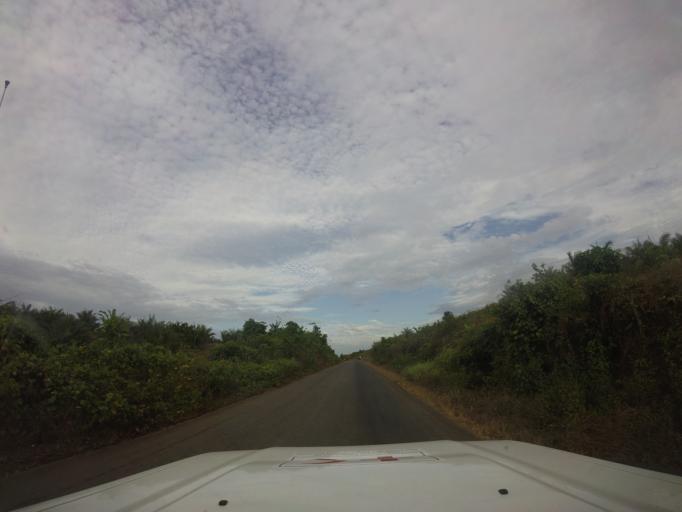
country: LR
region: Bomi
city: Tubmanburg
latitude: 6.7120
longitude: -10.9514
